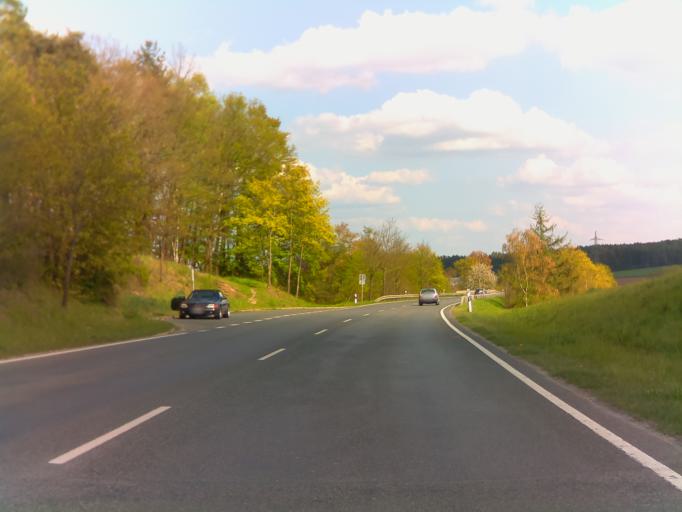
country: DE
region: Bavaria
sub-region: Upper Franconia
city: Neustadt bei Coburg
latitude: 50.3127
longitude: 11.0969
